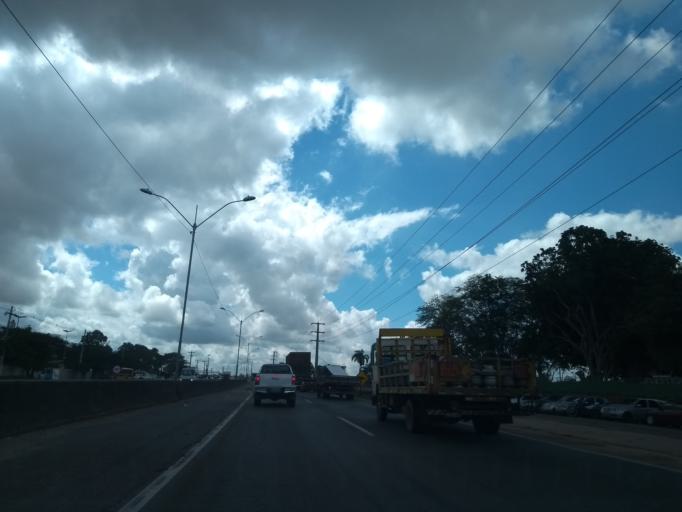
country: BR
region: Bahia
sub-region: Feira De Santana
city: Feira de Santana
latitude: -12.2793
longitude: -38.9416
